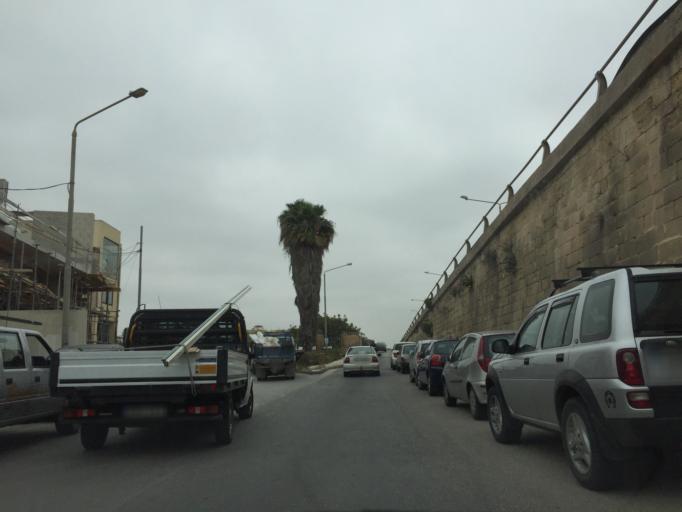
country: MT
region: Saint Venera
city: Santa Venera
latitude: 35.8839
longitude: 14.4729
